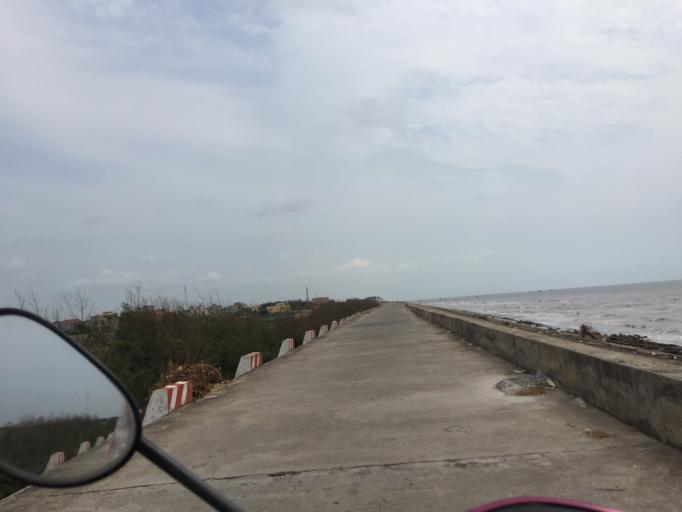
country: VN
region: Ninh Binh
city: Thi Tran Phat Diem
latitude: 20.0171
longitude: 106.2123
